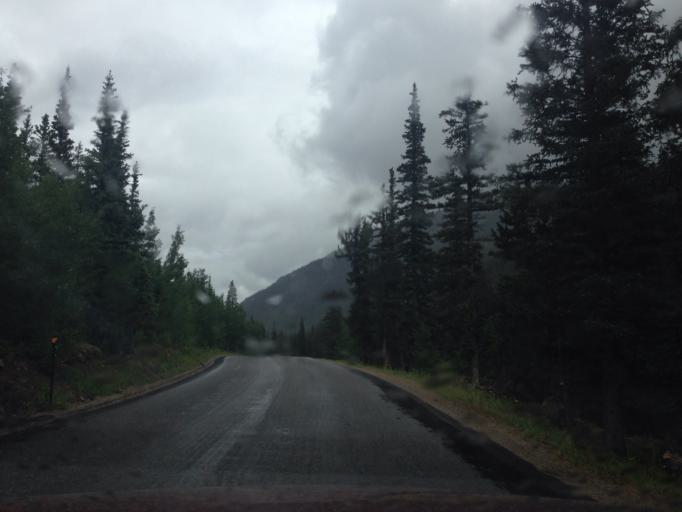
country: US
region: Colorado
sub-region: Clear Creek County
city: Georgetown
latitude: 39.6314
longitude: -105.7116
